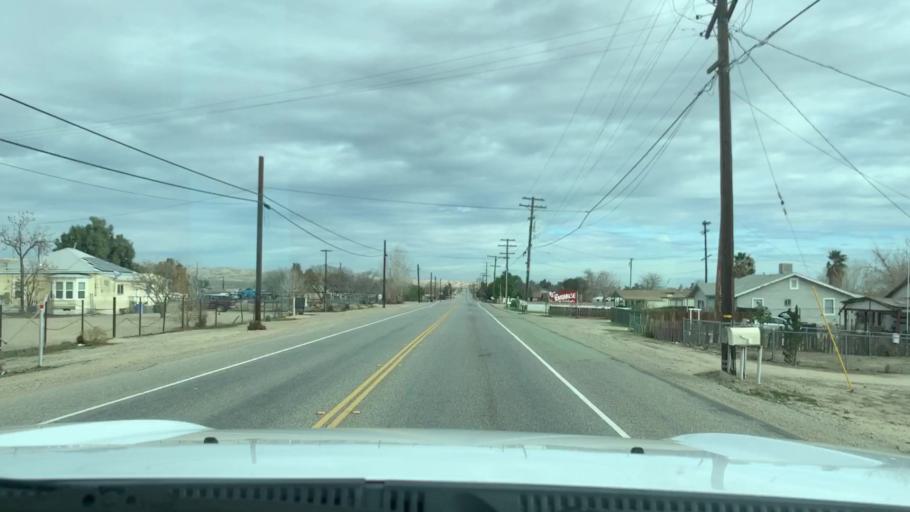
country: US
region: California
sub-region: Kern County
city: Ford City
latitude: 35.2189
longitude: -119.3913
